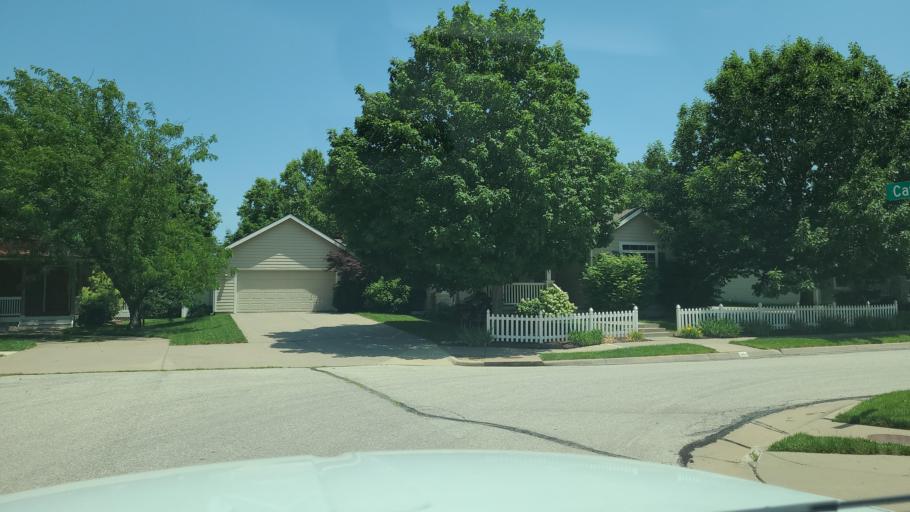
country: US
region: Kansas
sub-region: Douglas County
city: Lawrence
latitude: 38.9755
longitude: -95.2950
